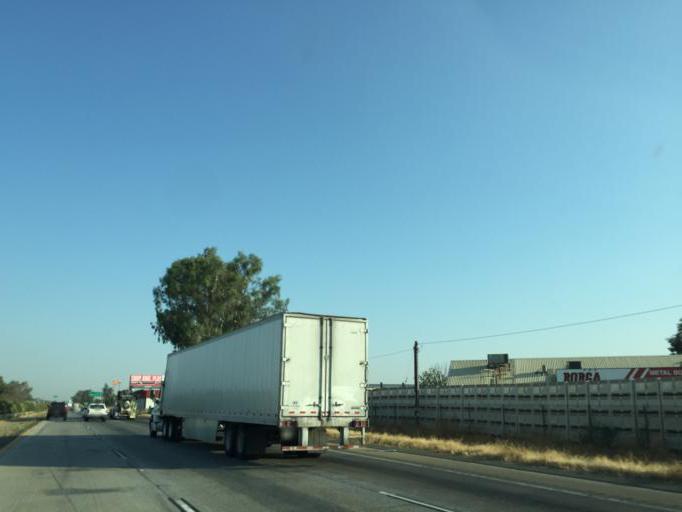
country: US
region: California
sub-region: Fresno County
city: Fowler
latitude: 36.6213
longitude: -119.6785
